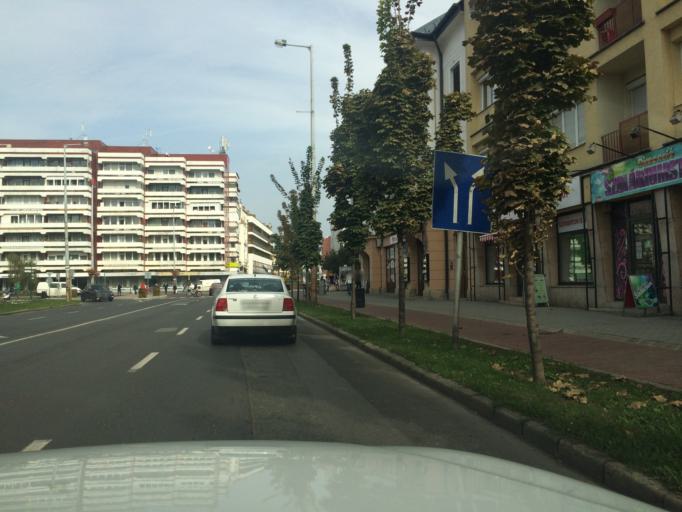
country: HU
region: Szabolcs-Szatmar-Bereg
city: Nyiregyhaza
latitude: 47.9533
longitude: 21.7157
